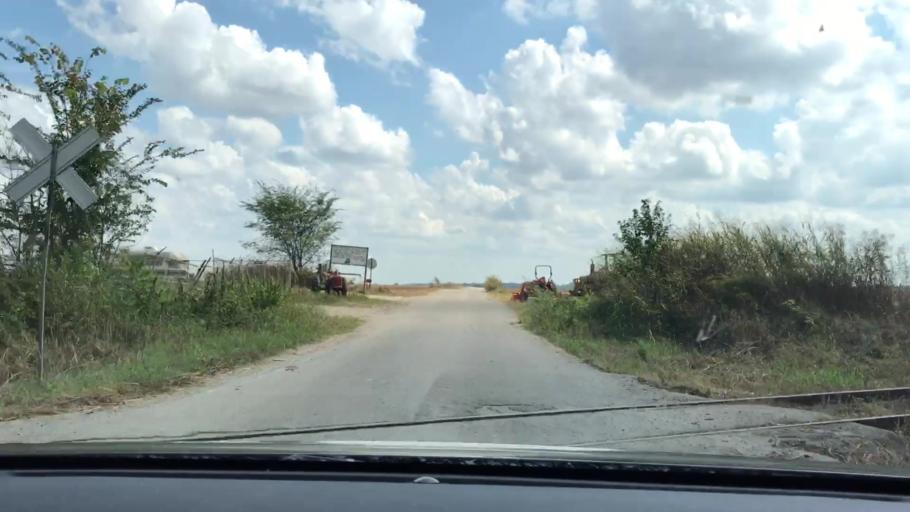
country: US
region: Kentucky
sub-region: Christian County
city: Oak Grove
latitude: 36.6832
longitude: -87.4417
